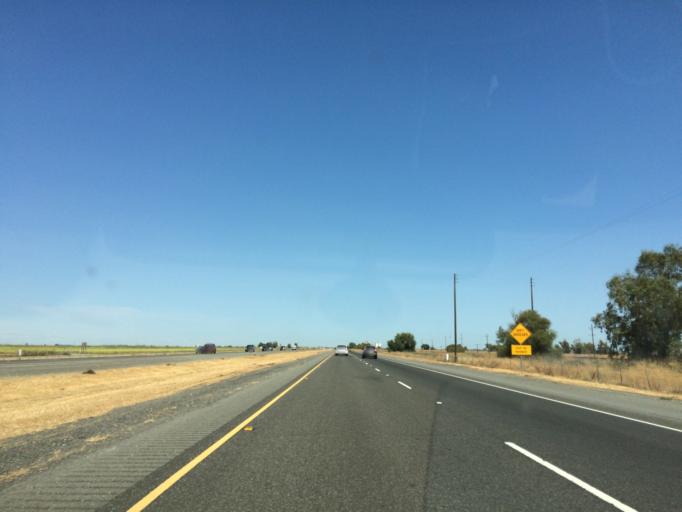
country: US
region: California
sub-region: Glenn County
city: Willows
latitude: 39.4422
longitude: -122.1934
